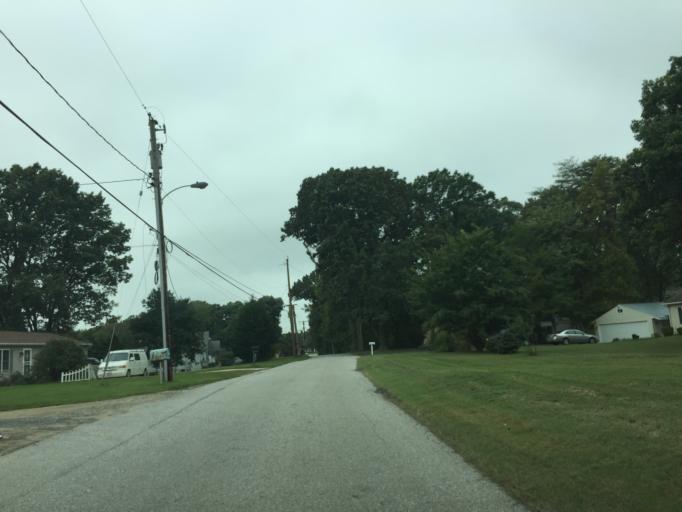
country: US
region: Maryland
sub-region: Baltimore County
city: Middle River
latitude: 39.3434
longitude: -76.4299
